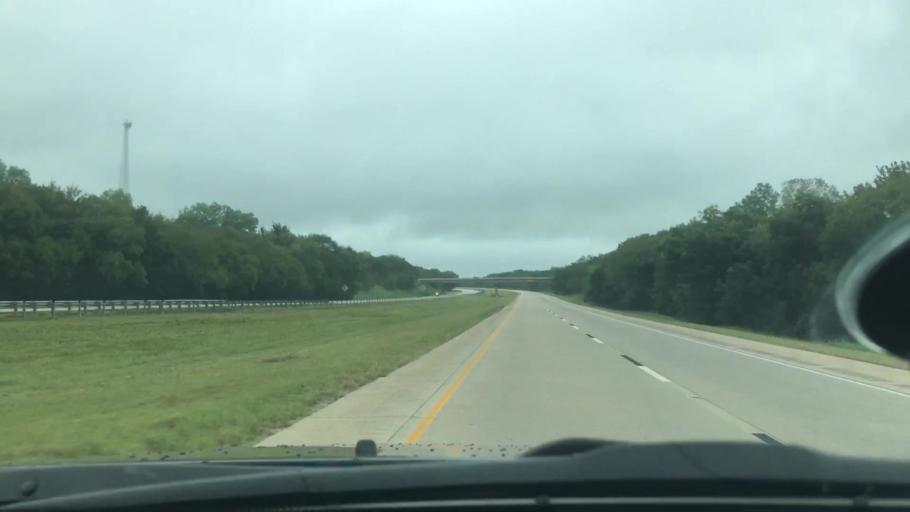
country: US
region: Oklahoma
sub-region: Okmulgee County
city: Henryetta
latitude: 35.4303
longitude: -95.9151
